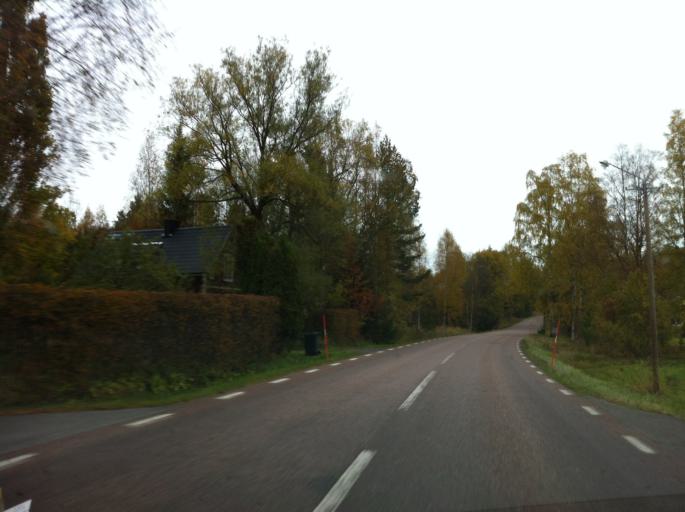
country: SE
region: Dalarna
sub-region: Ludvika Kommun
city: Grangesberg
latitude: 60.1569
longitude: 14.9736
